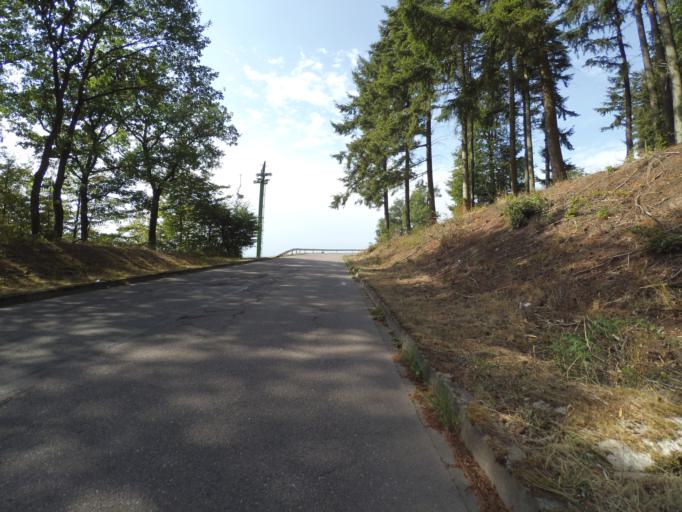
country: DE
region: Rheinland-Pfalz
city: Saarburg
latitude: 49.6130
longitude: 6.5473
